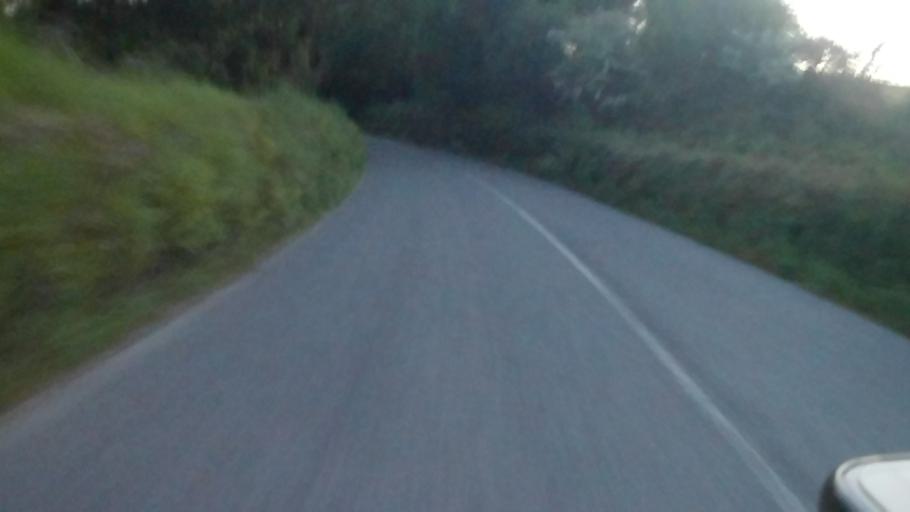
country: IE
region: Munster
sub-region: County Cork
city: Passage West
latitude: 51.9397
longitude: -8.3289
